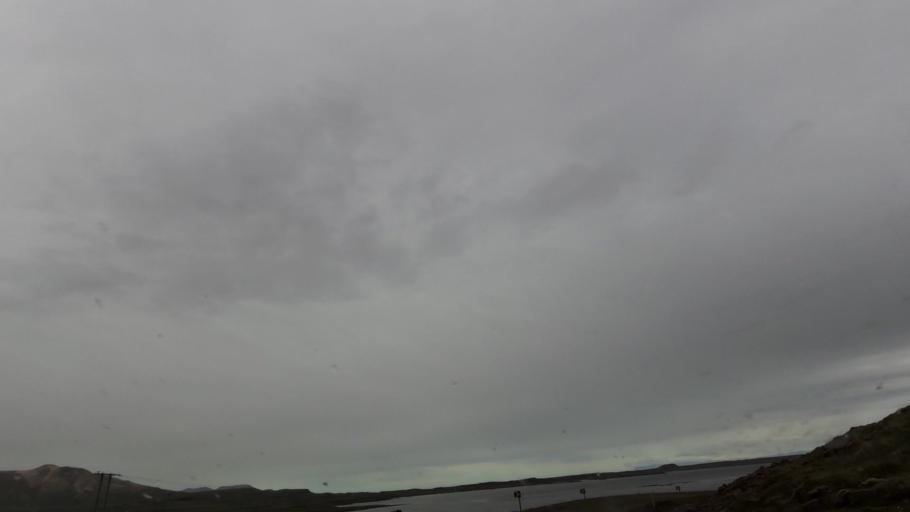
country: IS
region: West
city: Stykkisholmur
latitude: 64.9940
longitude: -22.5983
